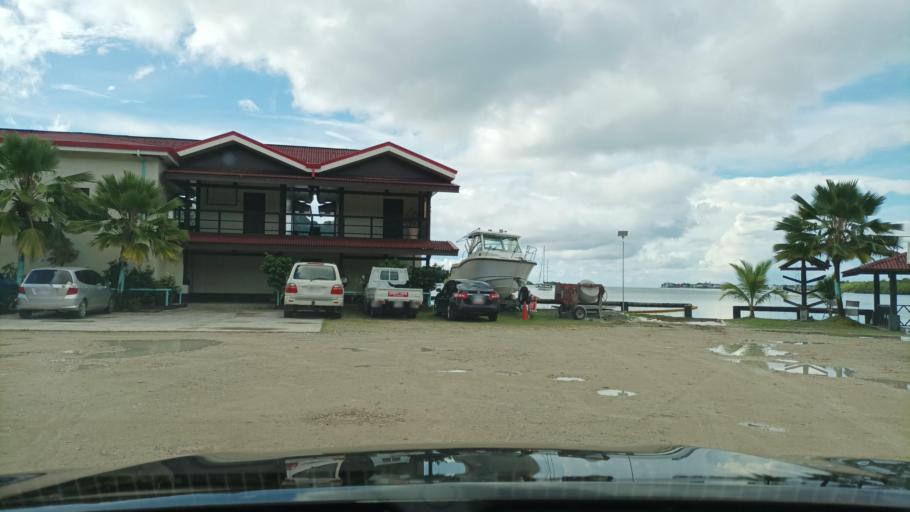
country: FM
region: Pohnpei
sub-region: Kolonia Municipality
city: Kolonia Town
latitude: 6.9590
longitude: 158.2014
